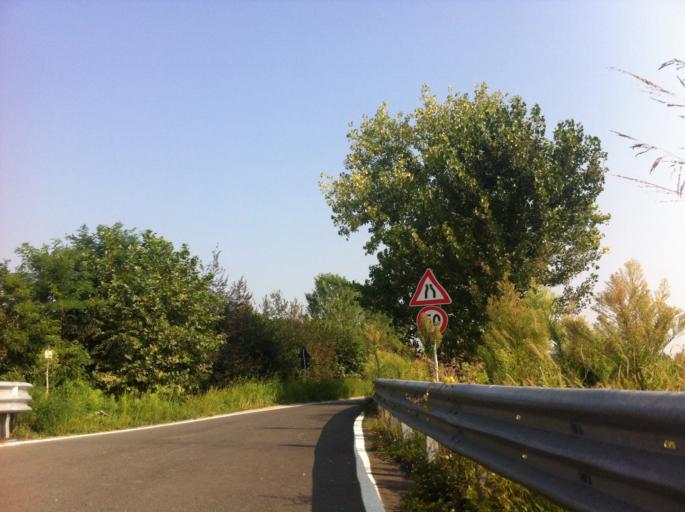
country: IT
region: Lombardy
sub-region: Provincia di Lodi
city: Tavazzano
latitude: 45.3396
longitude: 9.4111
